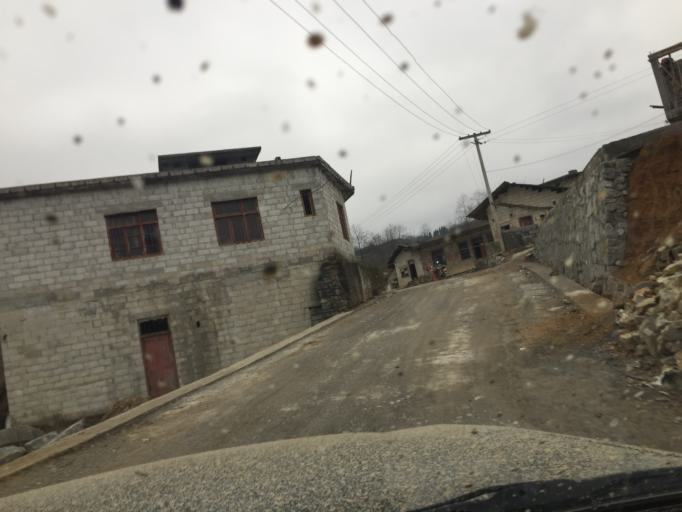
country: CN
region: Guizhou Sheng
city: Changfeng
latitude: 28.4925
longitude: 108.0522
